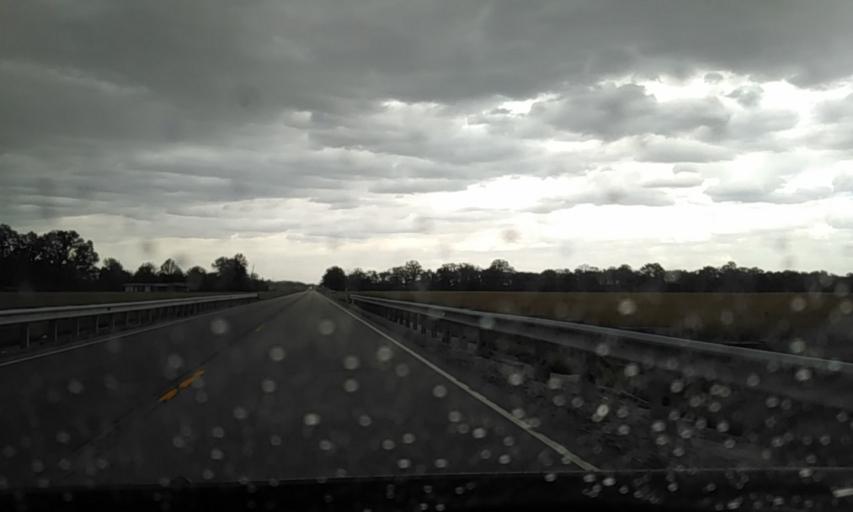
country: US
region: Illinois
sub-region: Bond County
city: Greenville
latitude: 38.8626
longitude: -89.4311
